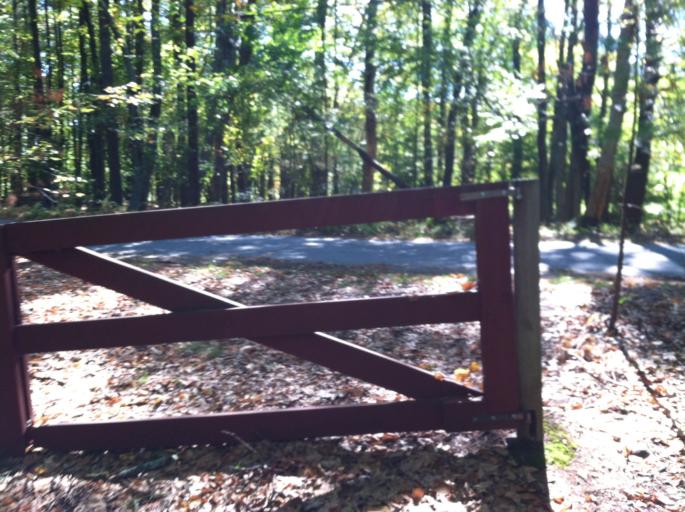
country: US
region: Massachusetts
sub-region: Middlesex County
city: Carlisle
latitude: 42.5313
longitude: -71.3559
